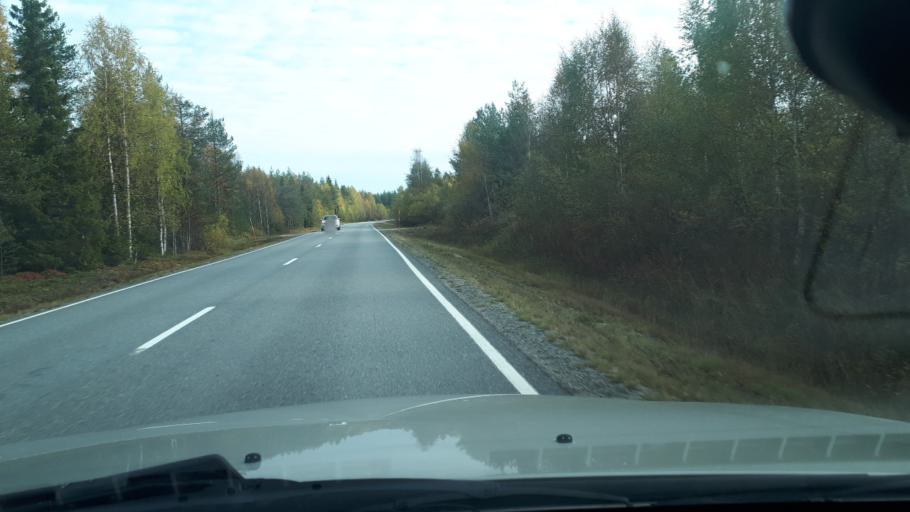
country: FI
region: Northern Ostrobothnia
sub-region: Oulu
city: Yli-Ii
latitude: 65.9230
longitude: 25.8078
